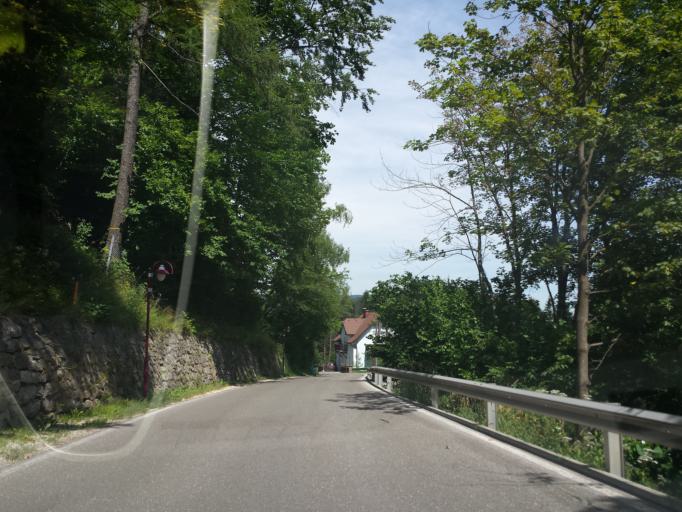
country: AT
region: Lower Austria
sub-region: Politischer Bezirk Neunkirchen
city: Semmering
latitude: 47.6349
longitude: 15.8341
